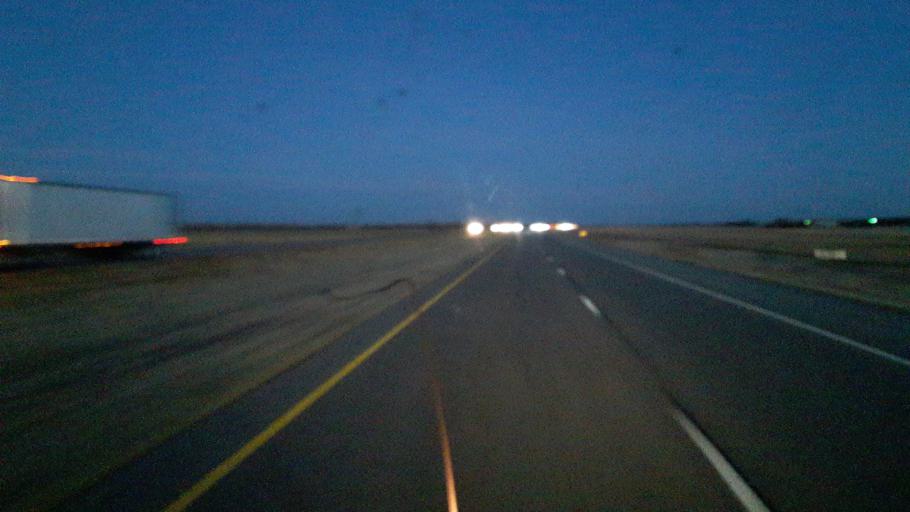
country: US
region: Nebraska
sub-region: Lincoln County
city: Sutherland
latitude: 41.1129
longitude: -101.3400
